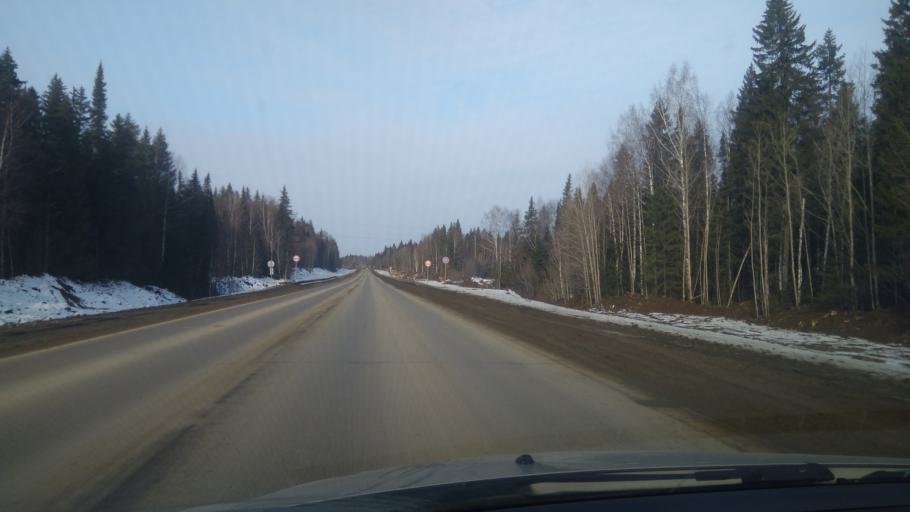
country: RU
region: Sverdlovsk
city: Bisert'
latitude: 56.8279
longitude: 59.1449
